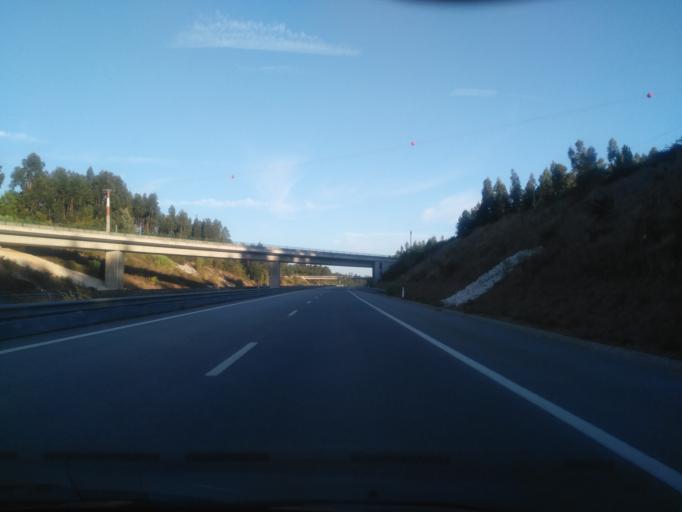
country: PT
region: Coimbra
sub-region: Figueira da Foz
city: Alhadas
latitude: 40.1734
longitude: -8.7942
